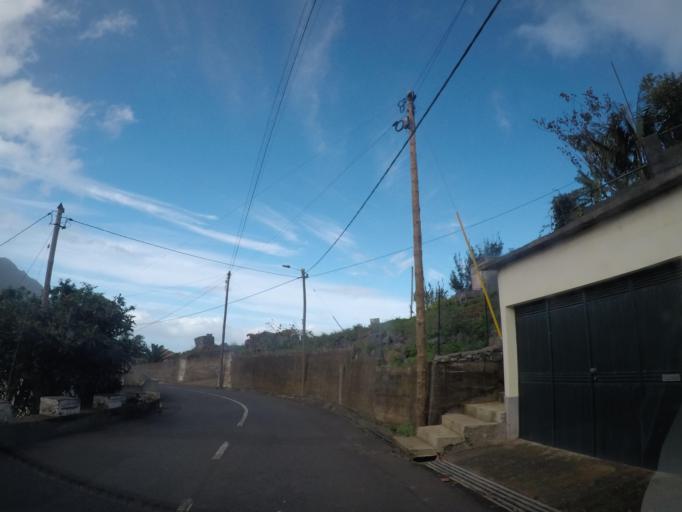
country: PT
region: Madeira
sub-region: Santana
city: Santana
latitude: 32.7872
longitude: -16.8474
